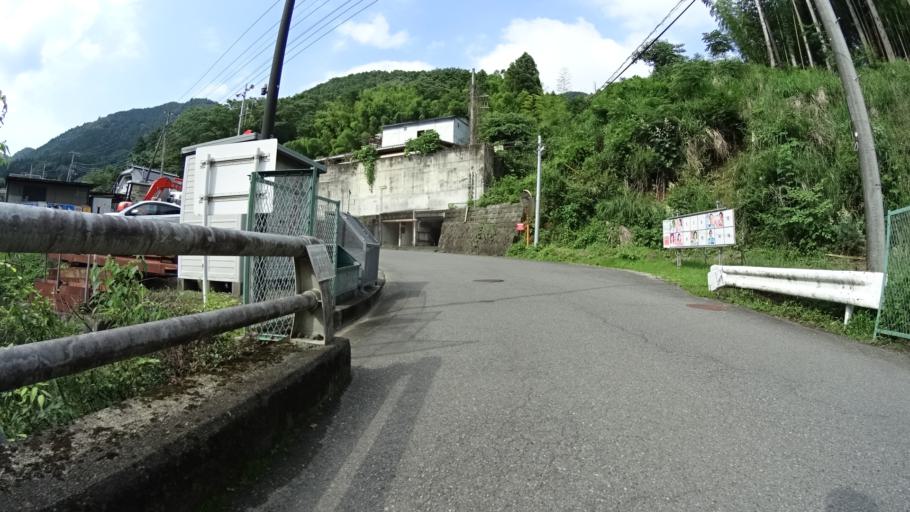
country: JP
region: Kanagawa
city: Atsugi
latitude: 35.4948
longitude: 139.2696
